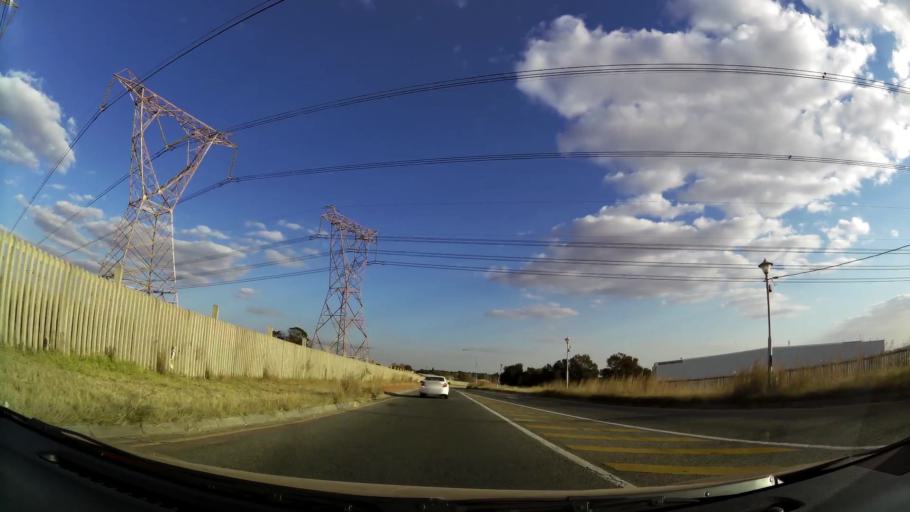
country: ZA
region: Gauteng
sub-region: City of Johannesburg Metropolitan Municipality
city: Midrand
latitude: -25.9254
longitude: 28.1579
